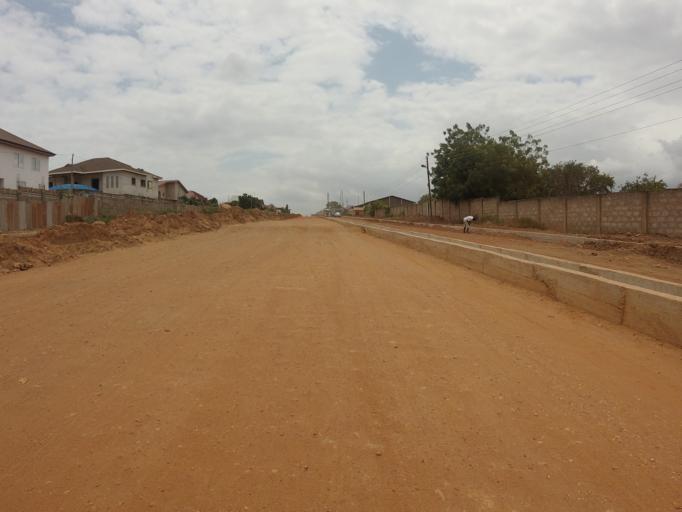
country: GH
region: Greater Accra
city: Medina Estates
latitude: 5.6293
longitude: -0.1425
